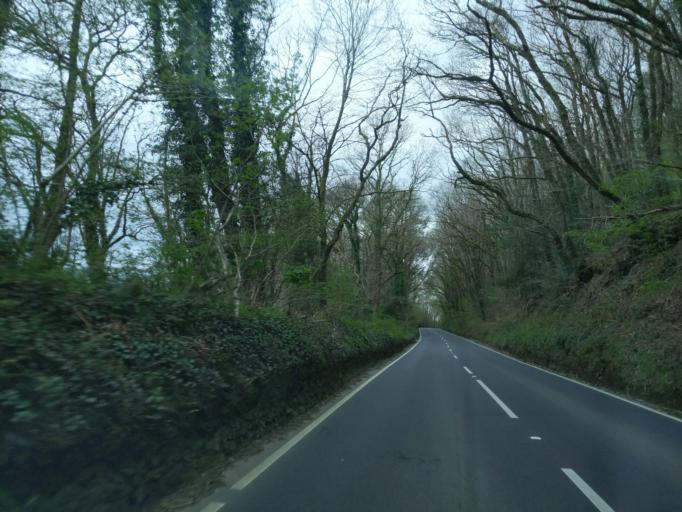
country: GB
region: England
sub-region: Devon
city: Great Torrington
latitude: 50.9346
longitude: -4.1070
